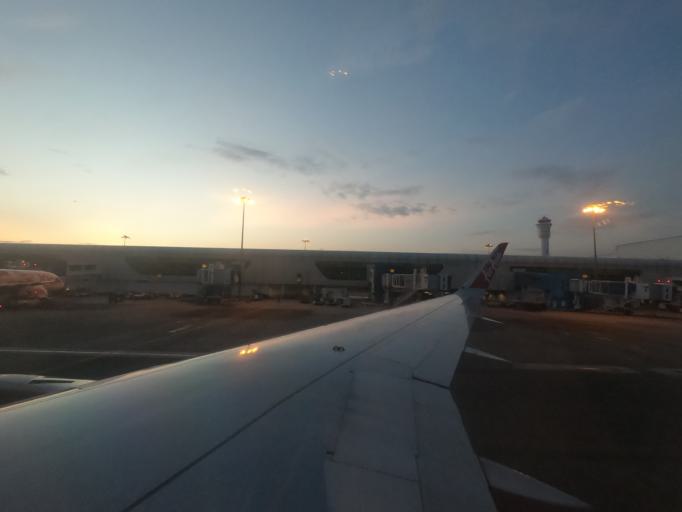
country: MY
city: Sungai Pelek New Village
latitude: 2.7402
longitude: 101.6852
